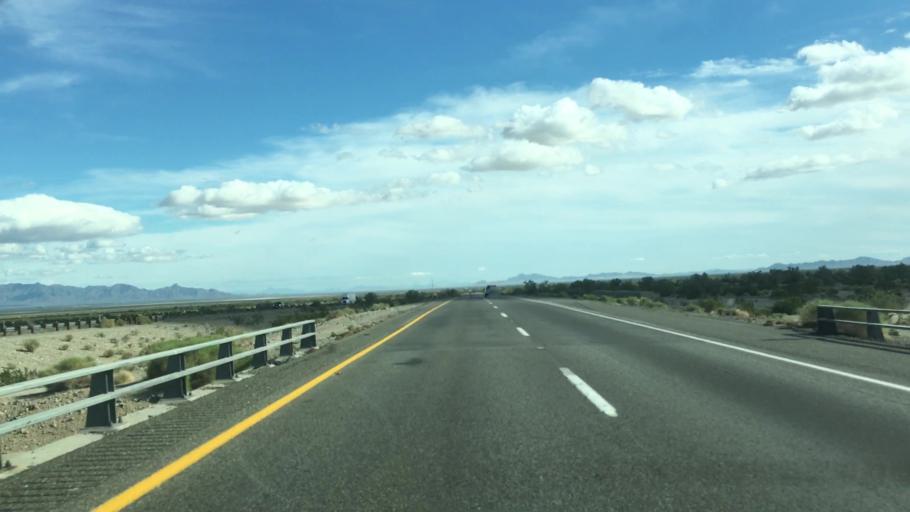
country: US
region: California
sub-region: Riverside County
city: Mesa Verde
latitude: 33.6572
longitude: -115.1585
